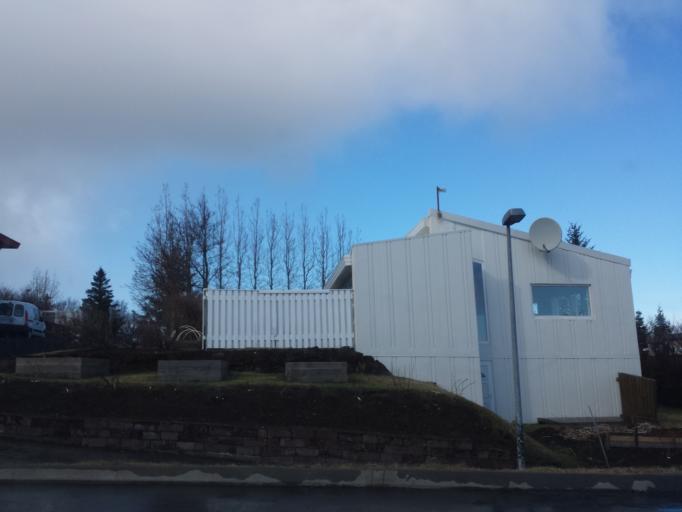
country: IS
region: Capital Region
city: Reykjavik
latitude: 64.1120
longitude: -21.8612
